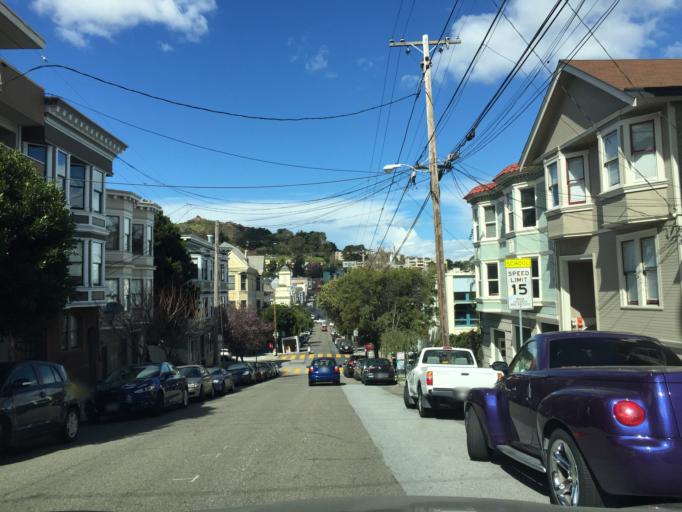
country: US
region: California
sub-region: San Francisco County
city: San Francisco
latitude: 37.7585
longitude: -122.4370
